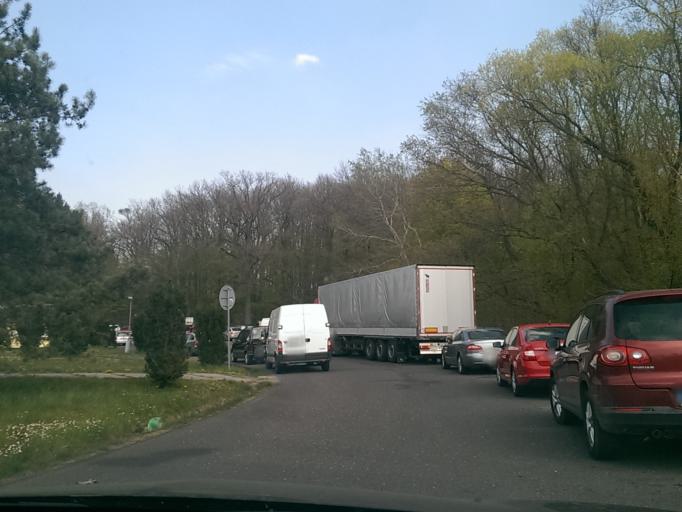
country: CZ
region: Central Bohemia
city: Bakov nad Jizerou
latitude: 50.4651
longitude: 14.9417
